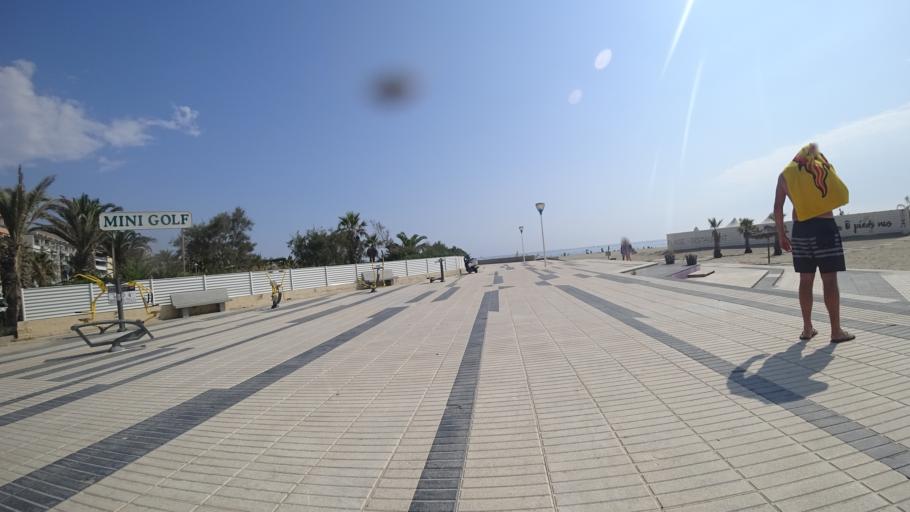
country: FR
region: Languedoc-Roussillon
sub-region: Departement des Pyrenees-Orientales
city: Canet-en-Roussillon
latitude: 42.6845
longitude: 3.0347
